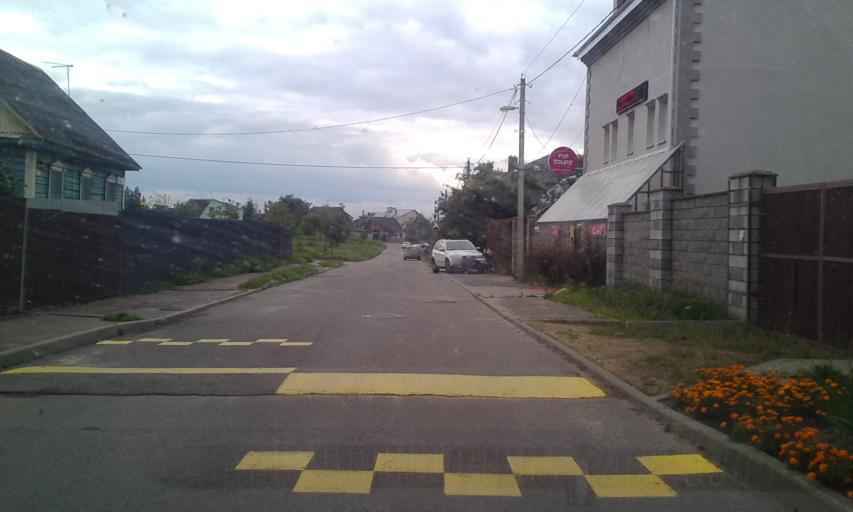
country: BY
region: Minsk
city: Minsk
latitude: 53.9464
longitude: 27.5758
